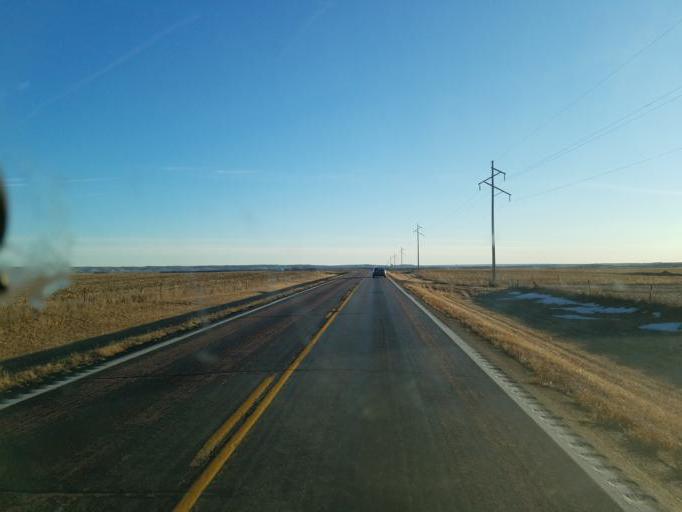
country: US
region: South Dakota
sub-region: Bon Homme County
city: Springfield
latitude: 42.9132
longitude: -97.8919
